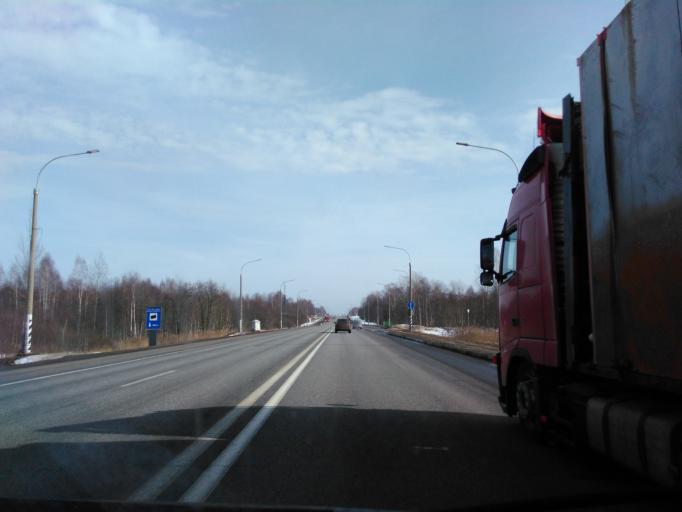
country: BY
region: Vitebsk
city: Dubrowna
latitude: 54.6903
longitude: 30.9549
